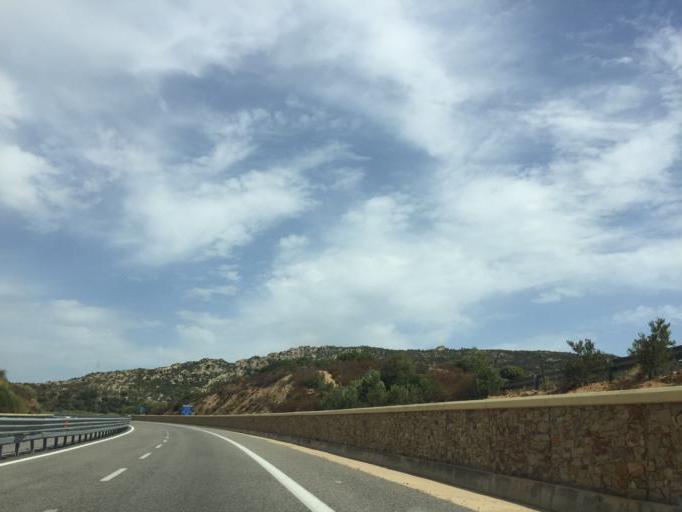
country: IT
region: Sardinia
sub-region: Provincia di Olbia-Tempio
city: San Teodoro
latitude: 40.7944
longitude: 9.6093
